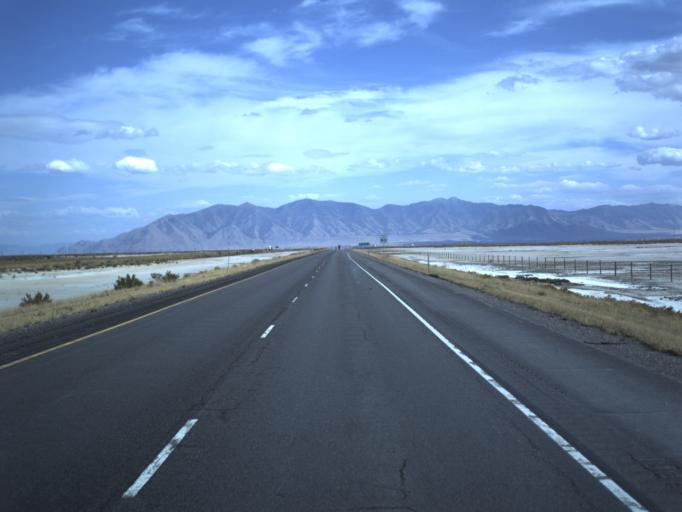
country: US
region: Utah
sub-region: Tooele County
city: Grantsville
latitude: 40.7050
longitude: -112.5142
